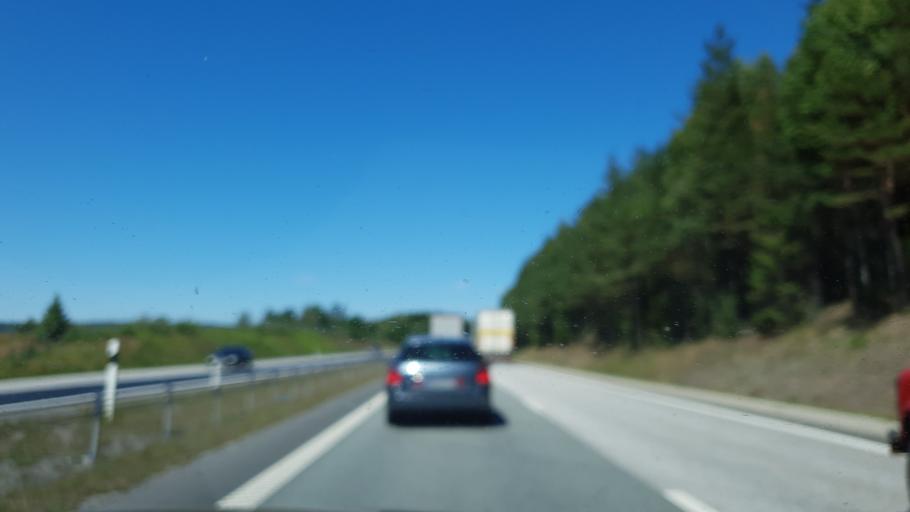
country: SE
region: Joenkoeping
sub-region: Jonkopings Kommun
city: Odensjo
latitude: 57.7243
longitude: 14.1597
